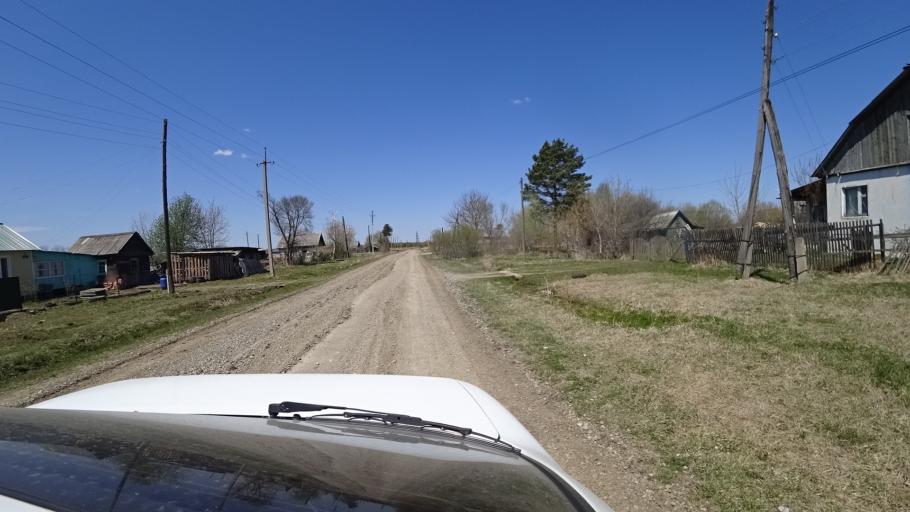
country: RU
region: Primorskiy
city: Lazo
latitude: 45.8001
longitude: 133.7632
